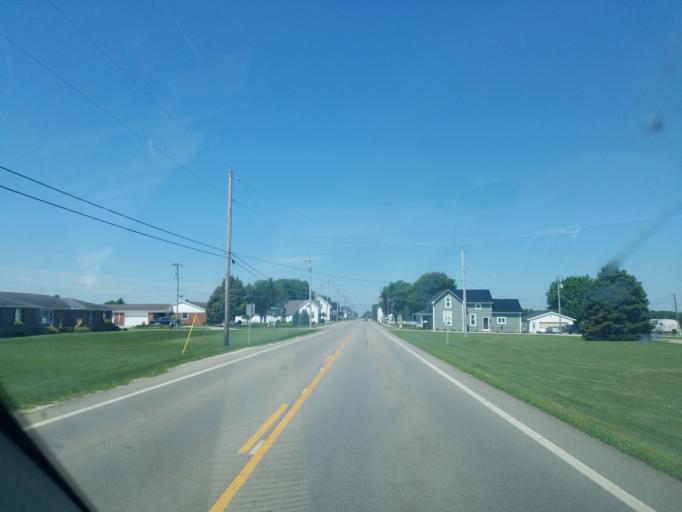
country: US
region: Ohio
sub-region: Auglaize County
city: Minster
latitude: 40.4076
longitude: -84.4639
